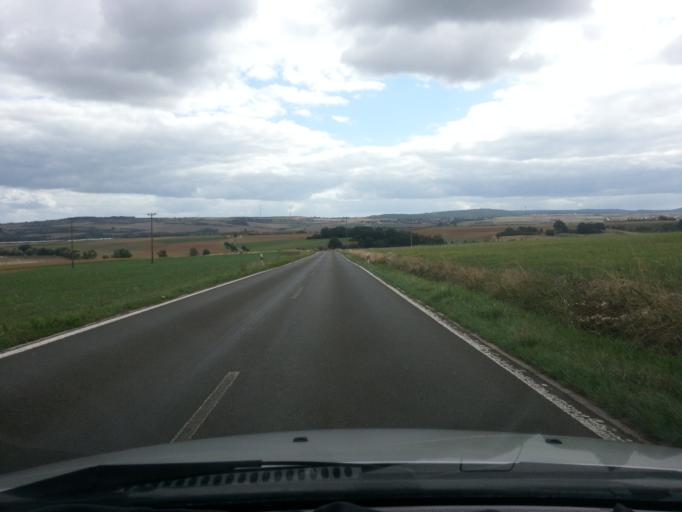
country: DE
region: Rheinland-Pfalz
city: Kerzenheim
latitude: 49.5760
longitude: 8.0684
